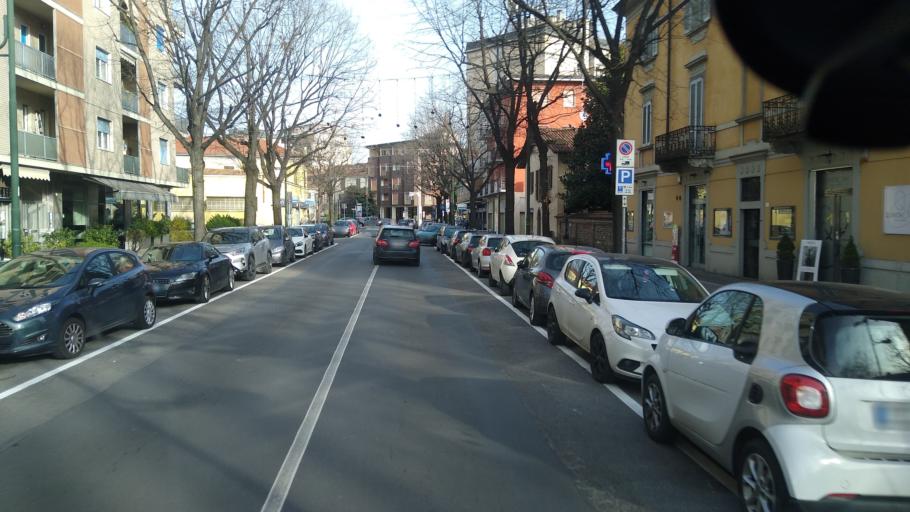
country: IT
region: Lombardy
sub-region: Provincia di Bergamo
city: Treviglio
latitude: 45.5181
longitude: 9.5904
